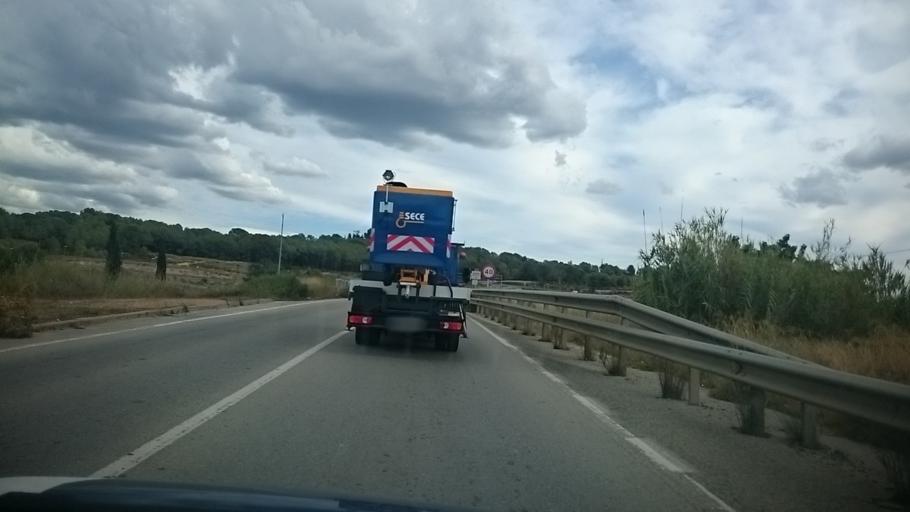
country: ES
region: Catalonia
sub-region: Provincia de Barcelona
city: Vilafranca del Penedes
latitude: 41.3324
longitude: 1.7102
